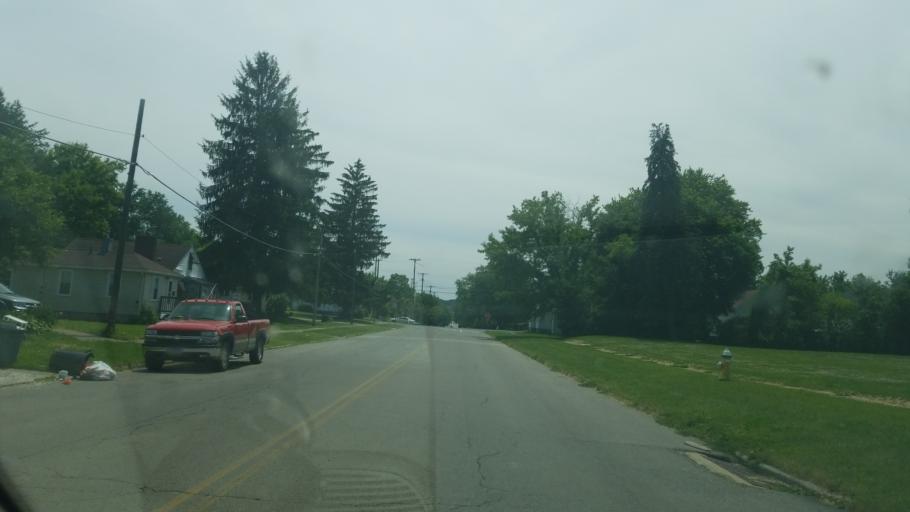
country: US
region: Ohio
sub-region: Richland County
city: Lincoln Heights
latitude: 40.7712
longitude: -82.5001
